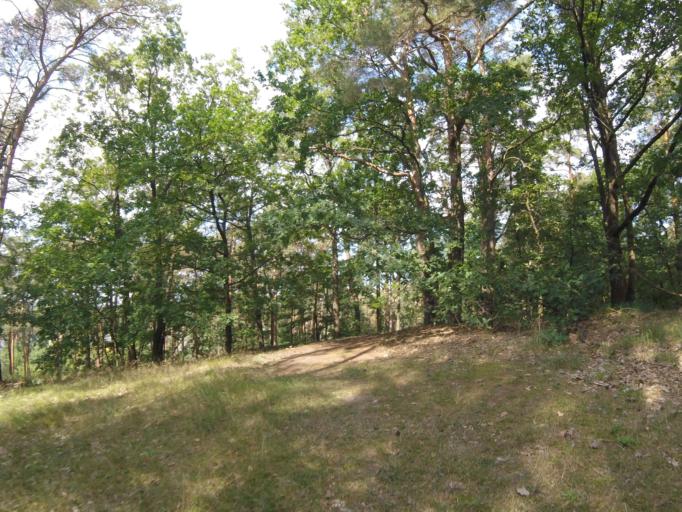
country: DE
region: Brandenburg
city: Konigs Wusterhausen
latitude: 52.2828
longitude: 13.6593
